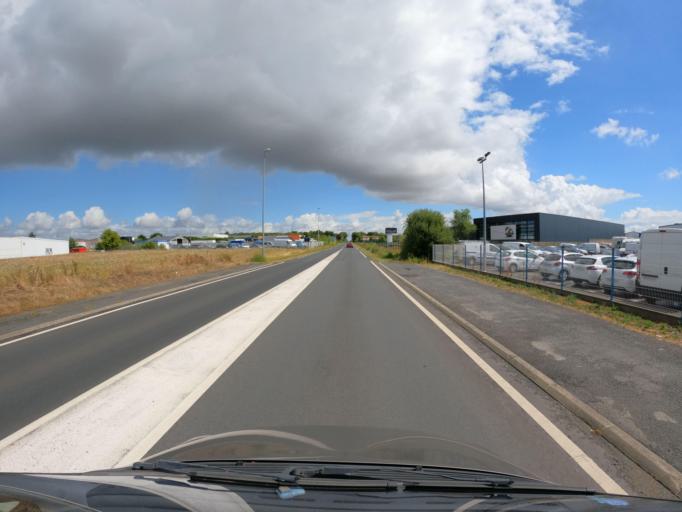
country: FR
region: Pays de la Loire
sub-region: Departement de la Loire-Atlantique
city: Vallet
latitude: 47.1798
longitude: -1.2590
